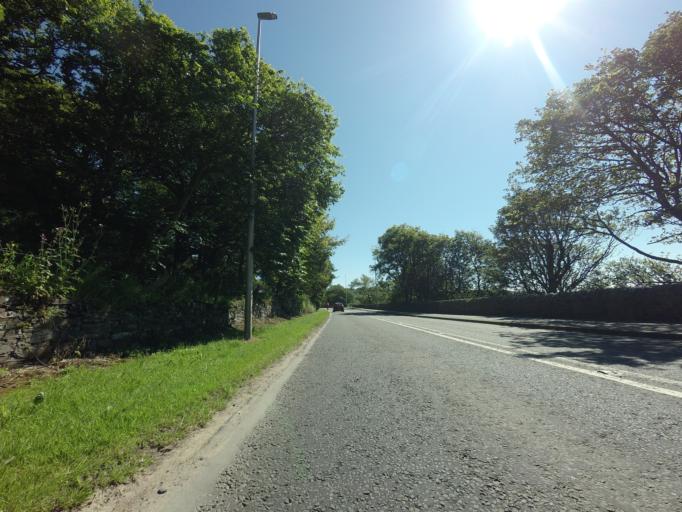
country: GB
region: Scotland
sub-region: Aberdeenshire
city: Macduff
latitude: 57.6607
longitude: -2.5116
